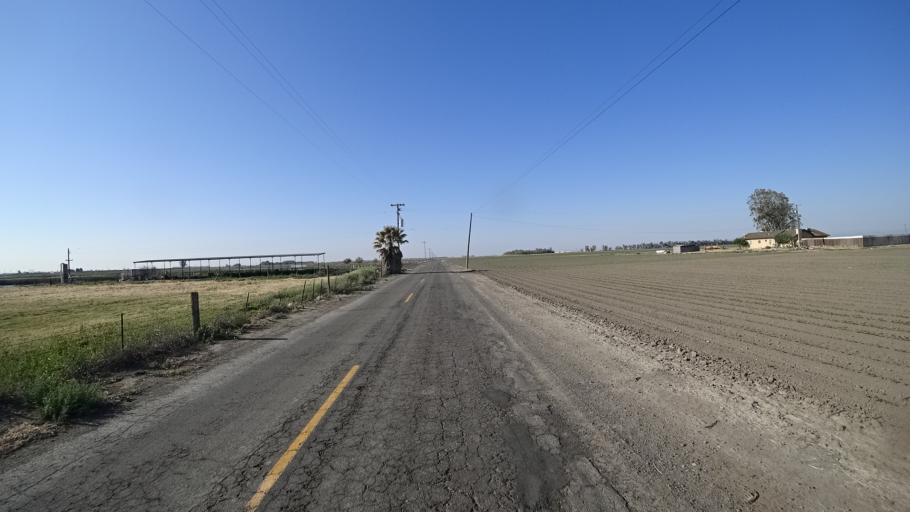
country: US
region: California
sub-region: Fresno County
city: Riverdale
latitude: 36.3883
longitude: -119.9277
